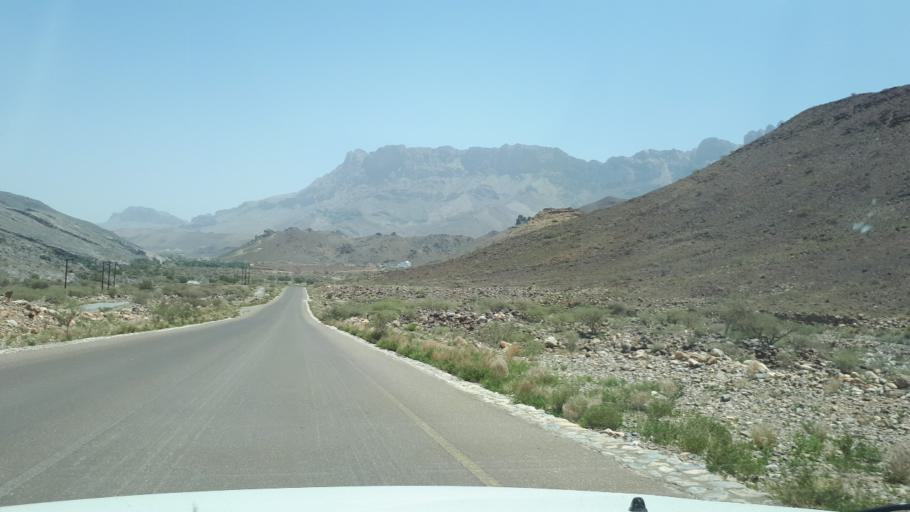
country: OM
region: Muhafazat ad Dakhiliyah
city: Bahla'
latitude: 23.1815
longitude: 57.1411
